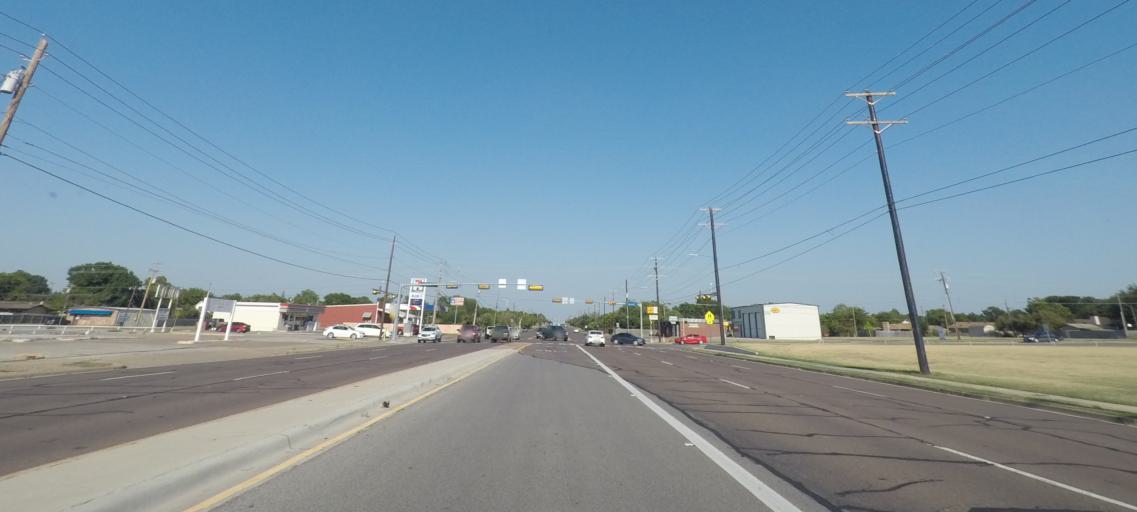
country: US
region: Texas
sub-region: Wichita County
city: Wichita Falls
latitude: 33.8581
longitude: -98.5789
